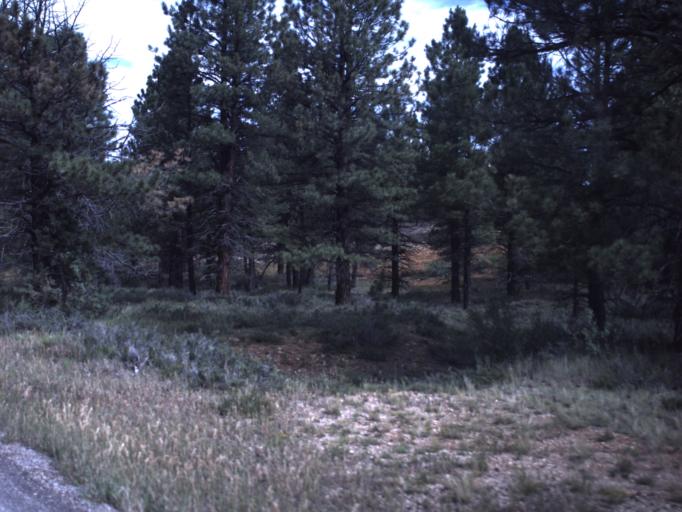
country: US
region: Utah
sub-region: Garfield County
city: Panguitch
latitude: 37.4975
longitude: -112.5871
